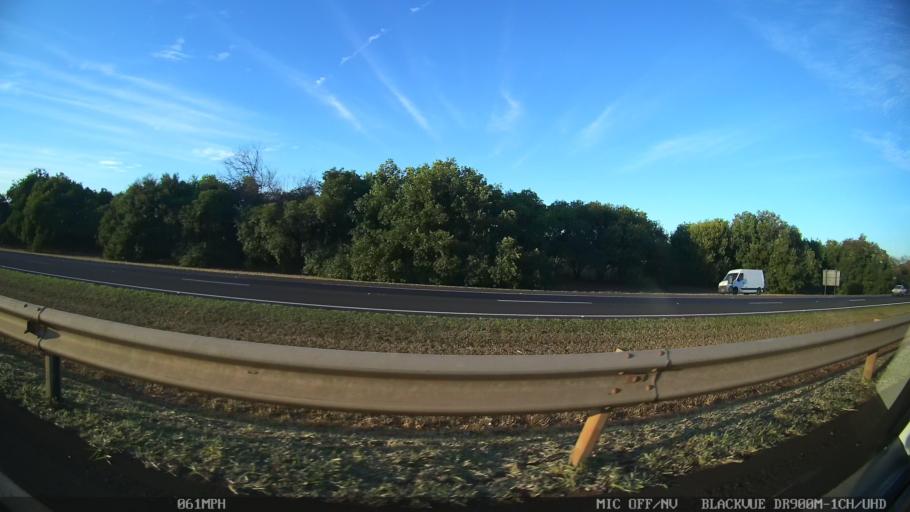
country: BR
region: Sao Paulo
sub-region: Catanduva
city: Catanduva
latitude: -21.1254
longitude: -49.0311
